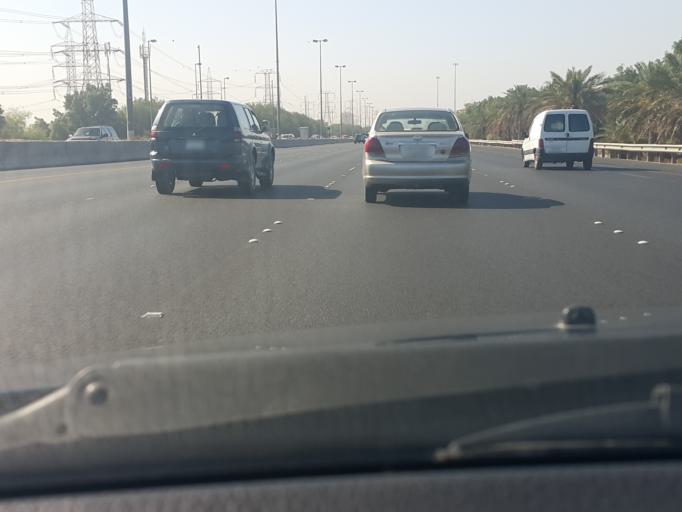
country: KW
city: Bayan
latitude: 29.2869
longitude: 48.0316
